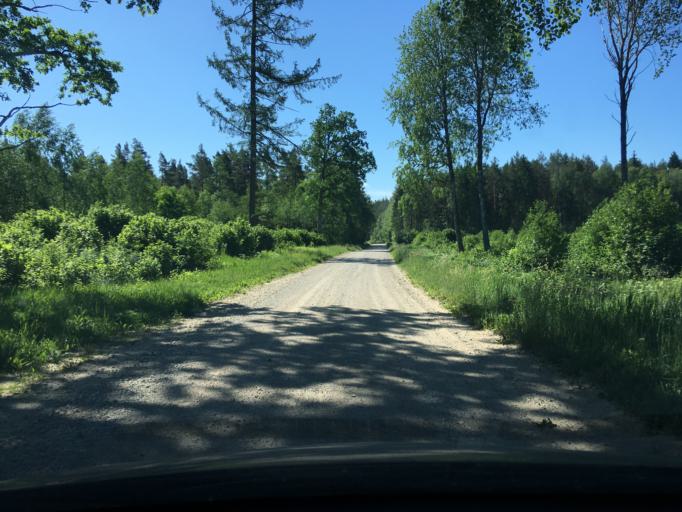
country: EE
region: Laeaene
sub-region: Lihula vald
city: Lihula
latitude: 58.6413
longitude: 23.7896
